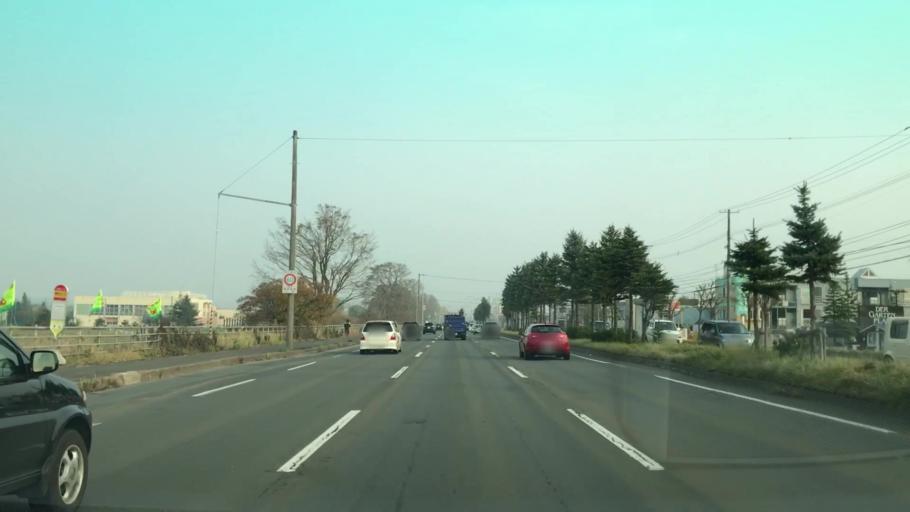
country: JP
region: Hokkaido
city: Sapporo
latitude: 43.1507
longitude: 141.3510
